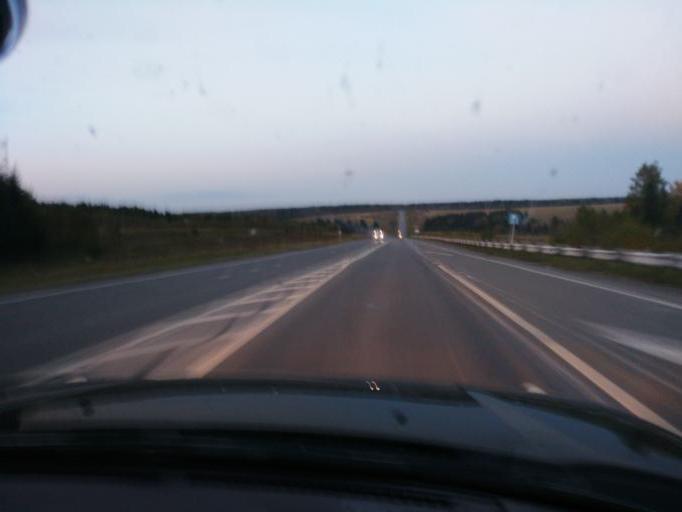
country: RU
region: Perm
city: Verkhnechusovskiye Gorodki
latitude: 58.2207
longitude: 57.1721
